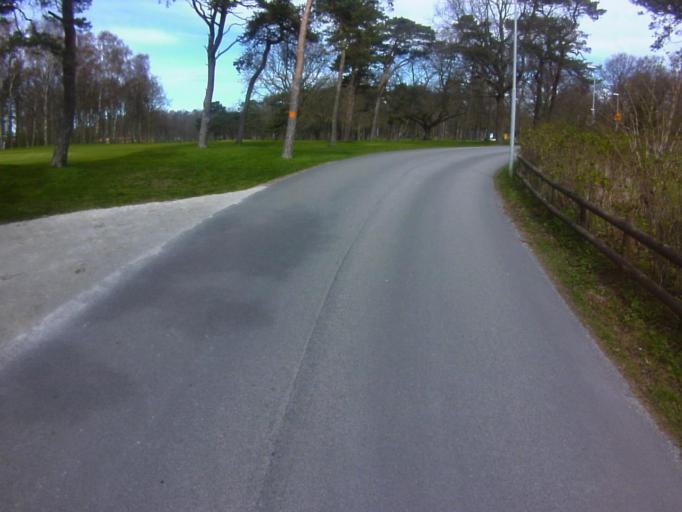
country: SE
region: Skane
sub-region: Kavlinge Kommun
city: Hofterup
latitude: 55.7894
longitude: 12.9463
